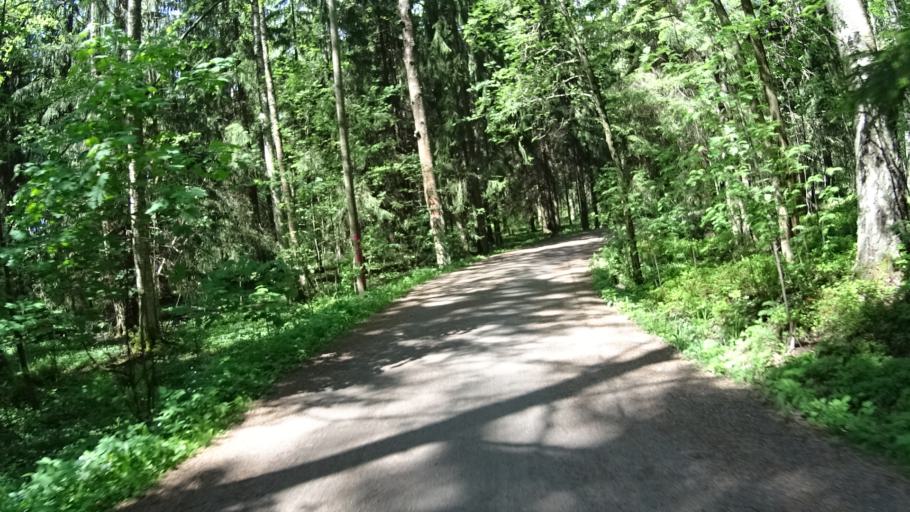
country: FI
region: Uusimaa
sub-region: Helsinki
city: Helsinki
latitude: 60.2270
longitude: 24.9147
